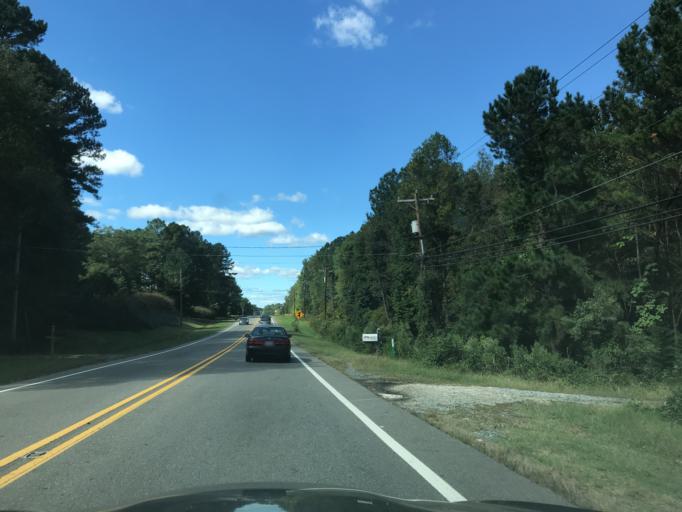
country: US
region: North Carolina
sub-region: Durham County
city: Gorman
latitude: 35.9773
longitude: -78.7973
